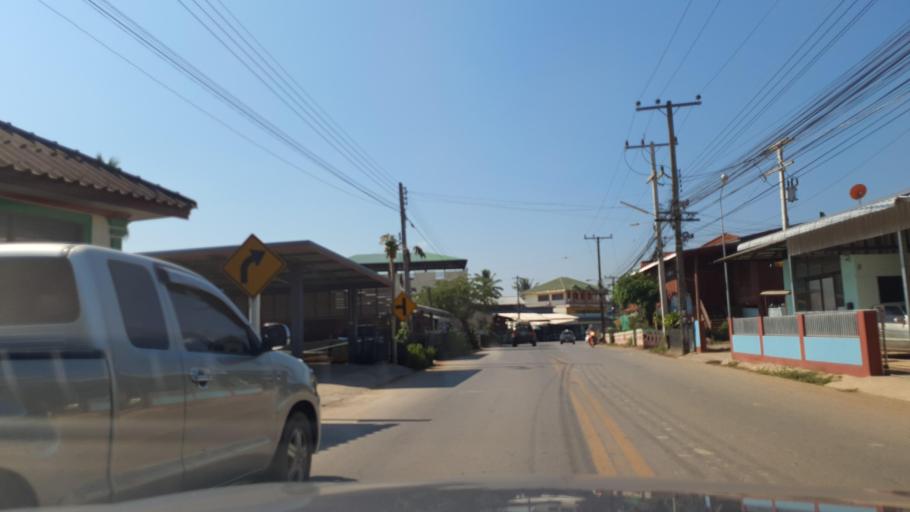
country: TH
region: Nan
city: Tha Wang Pha
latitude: 19.0845
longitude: 100.8912
